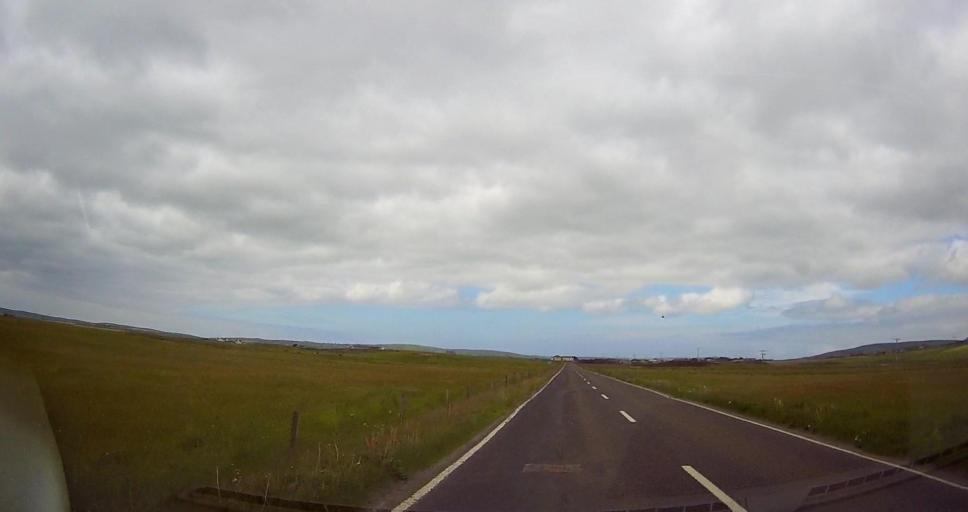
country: GB
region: Scotland
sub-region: Orkney Islands
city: Stromness
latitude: 59.0518
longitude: -3.2069
